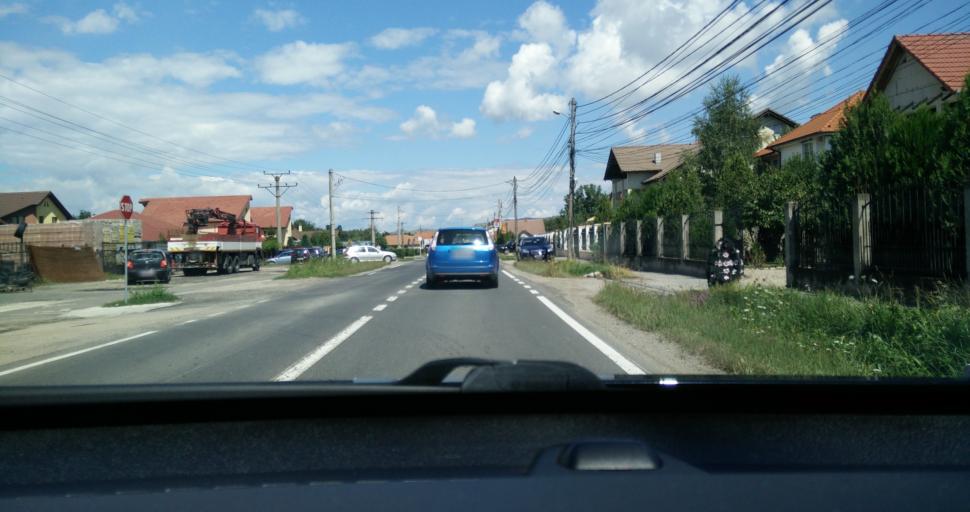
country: RO
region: Alba
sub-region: Municipiul Sebes
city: Sebes
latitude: 45.9411
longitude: 23.5632
